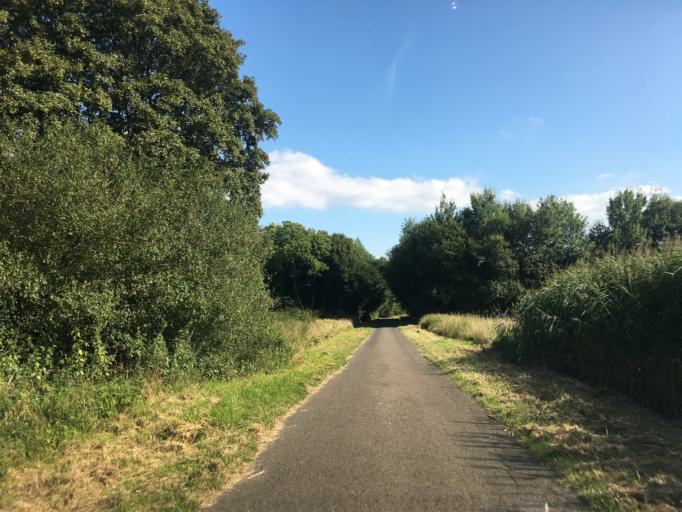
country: DE
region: North Rhine-Westphalia
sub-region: Regierungsbezirk Munster
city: Muenster
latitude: 52.0048
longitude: 7.5598
